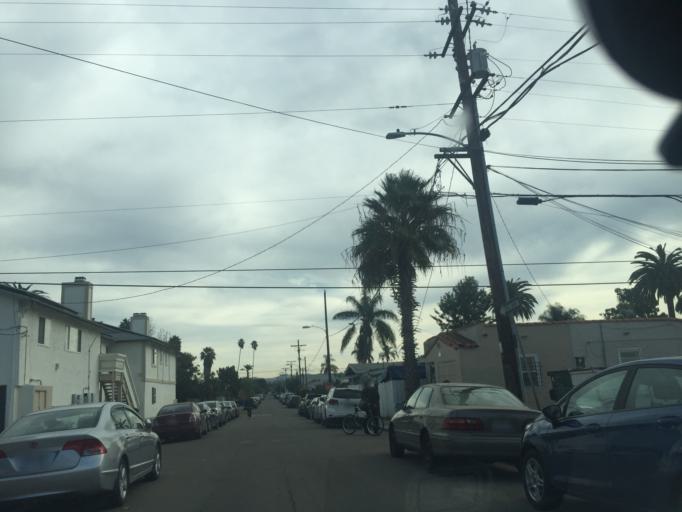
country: US
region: California
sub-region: San Diego County
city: San Diego
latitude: 32.7515
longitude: -117.1005
